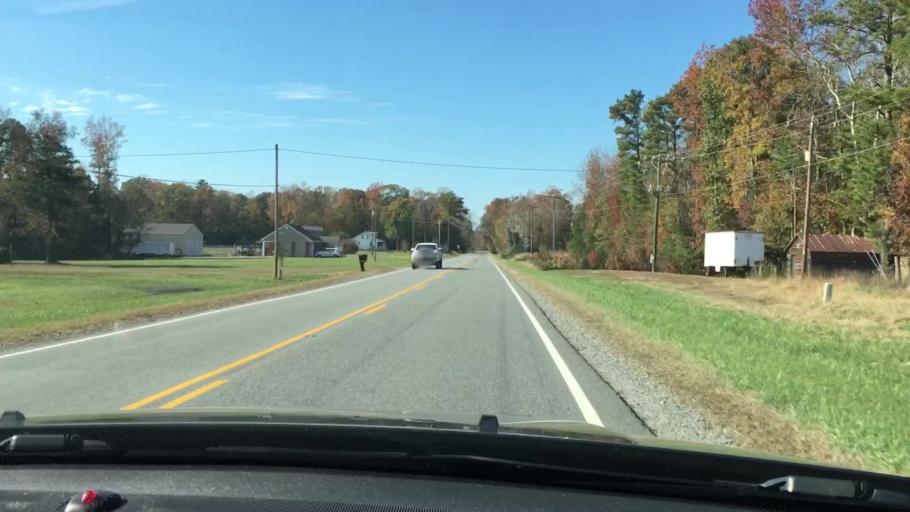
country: US
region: Virginia
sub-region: King William County
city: King William
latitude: 37.6729
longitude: -76.9758
